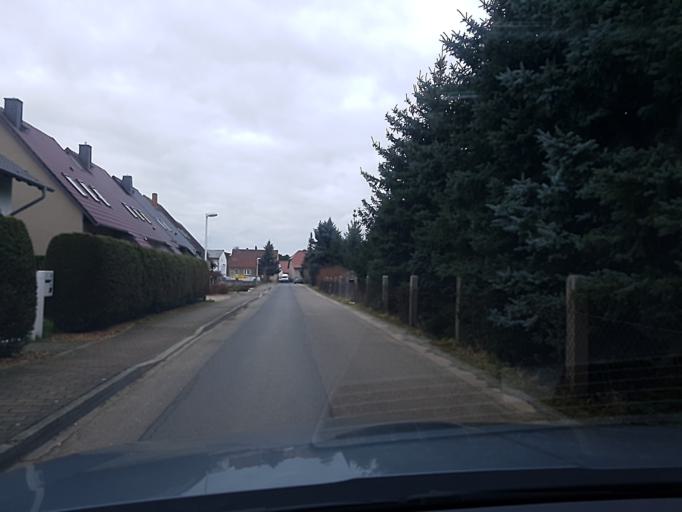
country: DE
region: Brandenburg
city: Bad Liebenwerda
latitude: 51.5460
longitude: 13.3619
